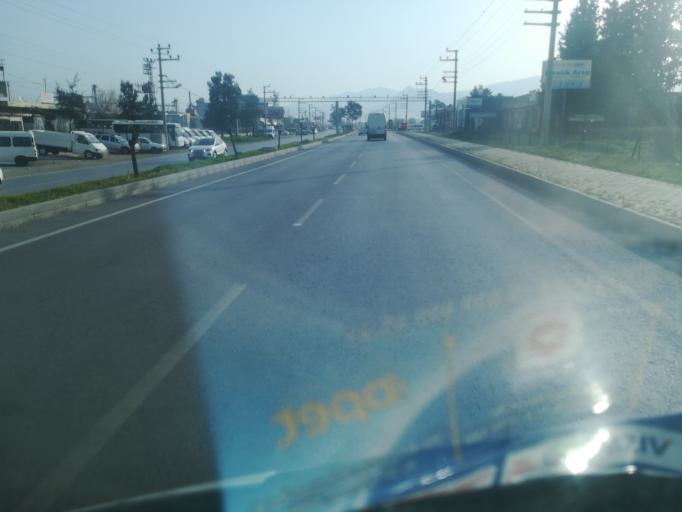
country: TR
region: Osmaniye
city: Osmaniye
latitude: 37.0571
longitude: 36.2106
